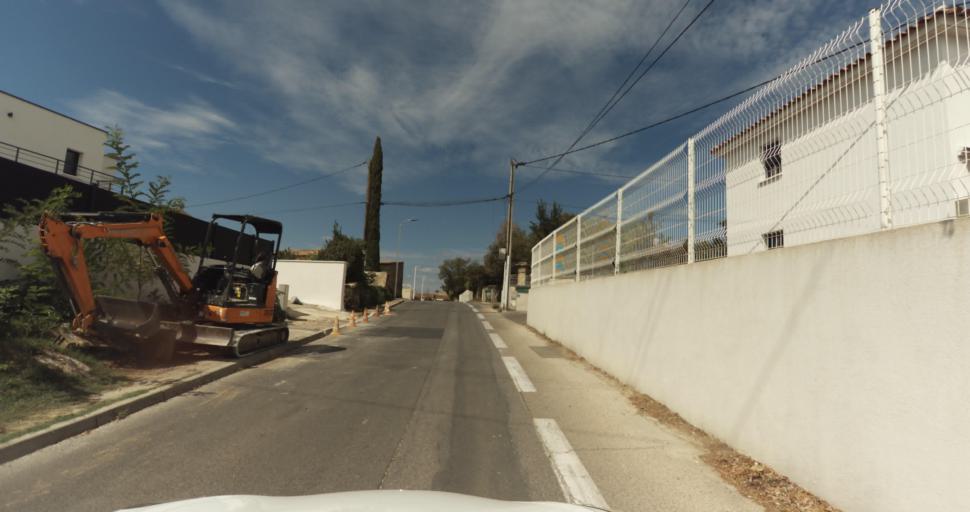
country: FR
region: Provence-Alpes-Cote d'Azur
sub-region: Departement des Bouches-du-Rhone
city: Miramas
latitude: 43.5796
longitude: 5.0144
